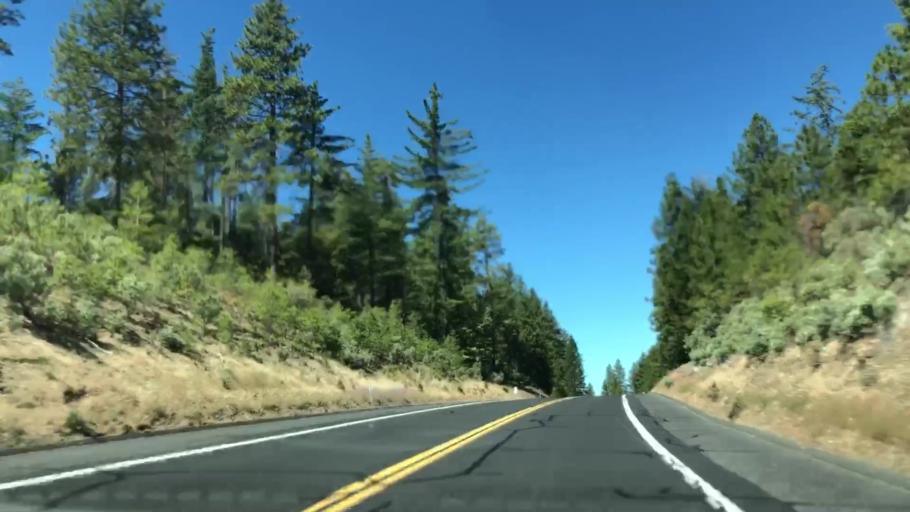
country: US
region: California
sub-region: Tuolumne County
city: Tuolumne City
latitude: 37.8259
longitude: -120.1758
